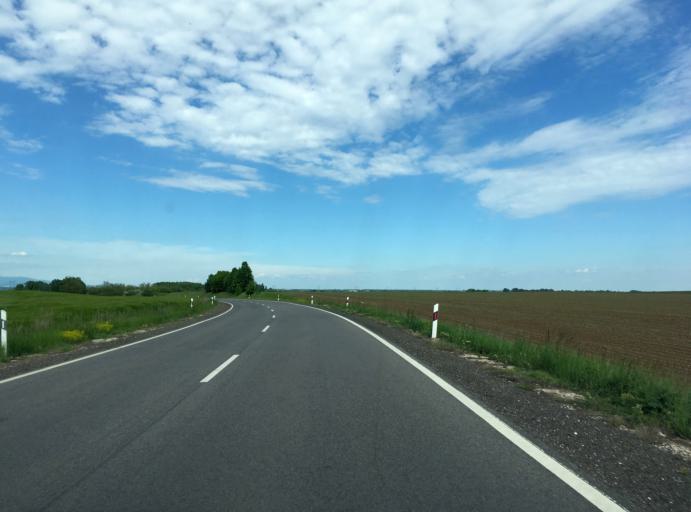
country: HU
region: Pest
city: Kartal
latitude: 47.6471
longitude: 19.5494
